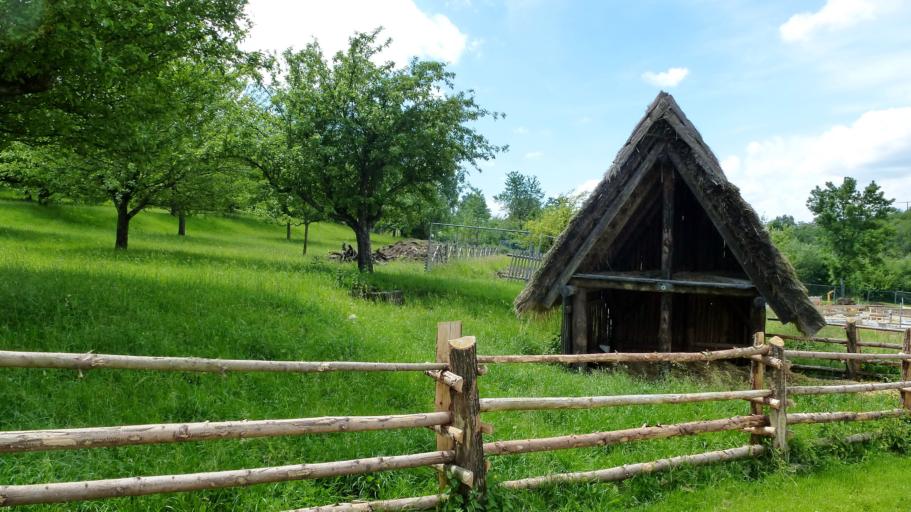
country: DE
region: Baden-Wuerttemberg
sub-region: Regierungsbezirk Stuttgart
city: Beuren
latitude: 48.5760
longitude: 9.4151
